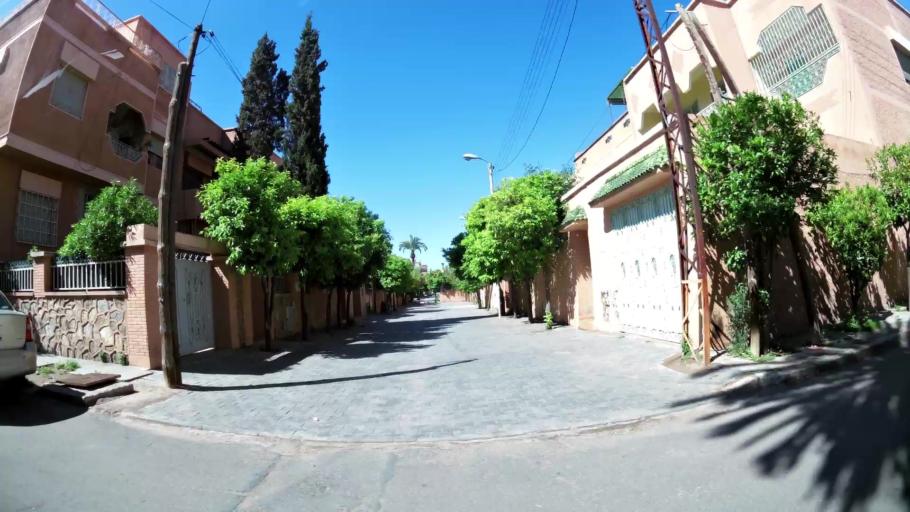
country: MA
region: Marrakech-Tensift-Al Haouz
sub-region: Marrakech
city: Marrakesh
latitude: 31.6443
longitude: -8.0104
